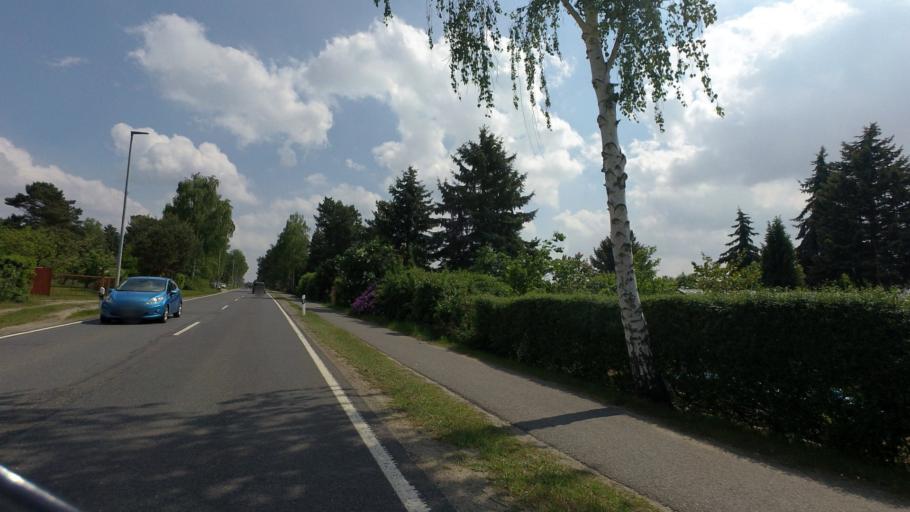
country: DE
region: Saxony
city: Weisswasser
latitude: 51.4947
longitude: 14.6484
